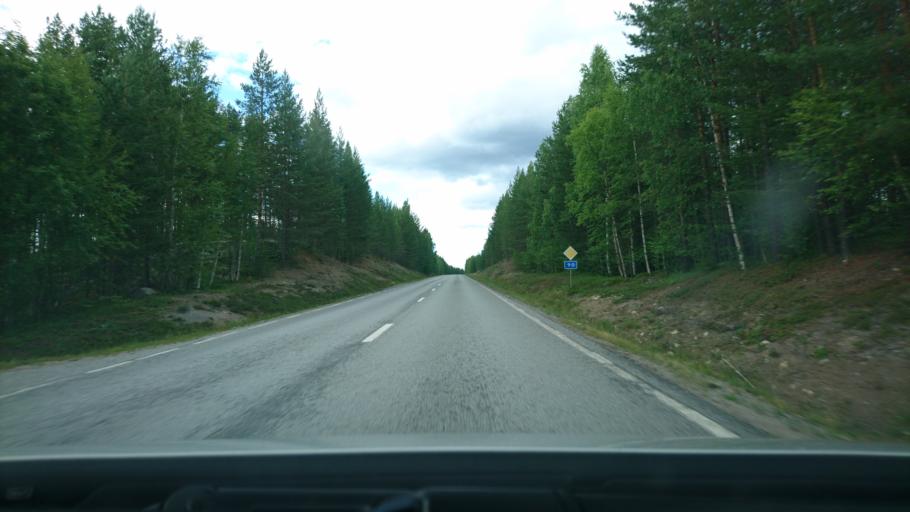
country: SE
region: Vaesterbotten
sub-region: Asele Kommun
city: Asele
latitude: 63.8785
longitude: 17.2041
